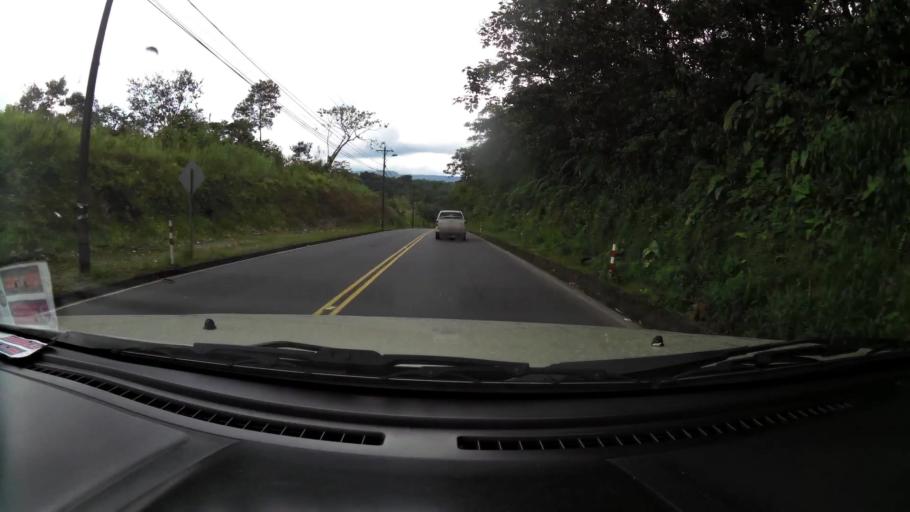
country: EC
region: Pastaza
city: Puyo
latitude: -1.4652
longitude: -78.1078
